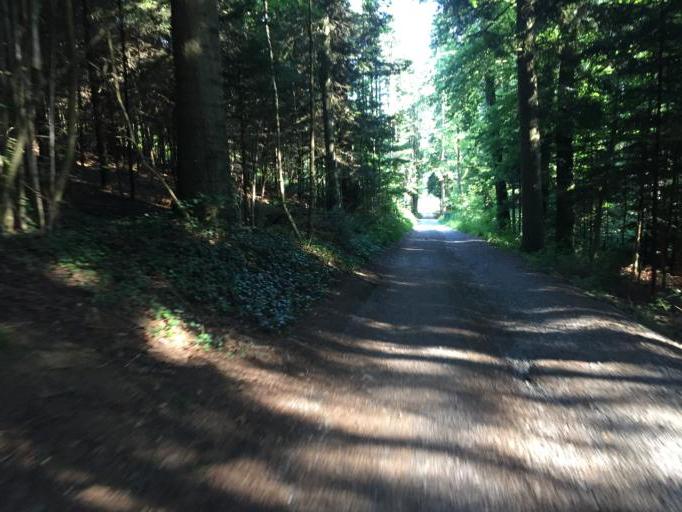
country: CH
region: Bern
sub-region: Bern-Mittelland District
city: Niederwichtrach
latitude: 46.8589
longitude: 7.5870
